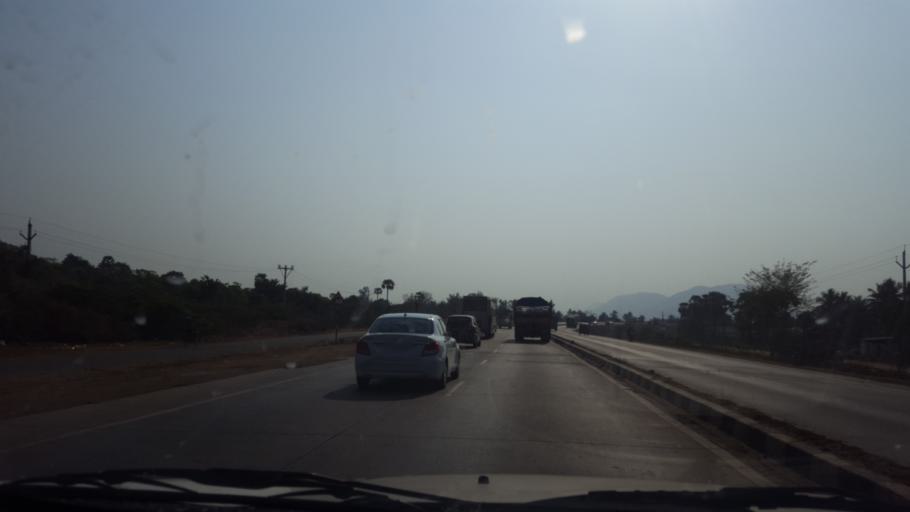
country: IN
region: Andhra Pradesh
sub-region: Vishakhapatnam
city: Anakapalle
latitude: 17.6523
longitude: 82.9252
